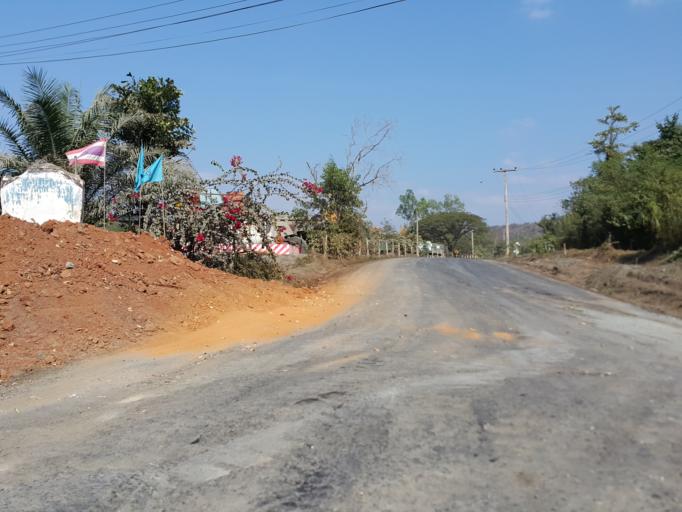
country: TH
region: Chiang Mai
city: Mae On
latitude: 18.8371
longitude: 99.2141
